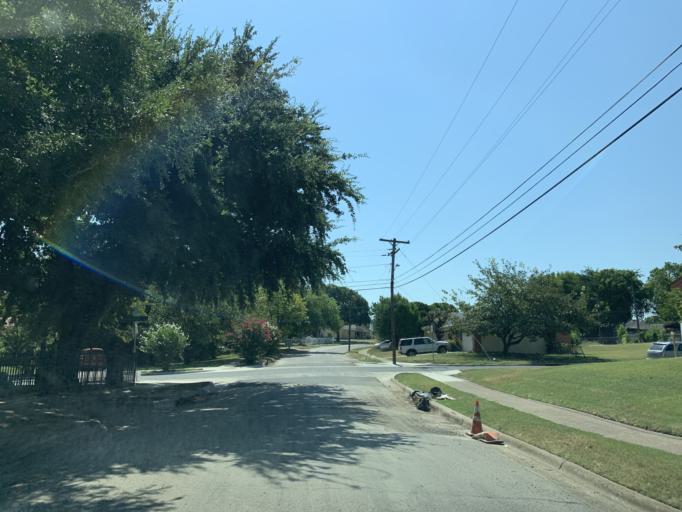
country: US
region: Texas
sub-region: Dallas County
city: Hutchins
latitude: 32.6740
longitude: -96.7561
